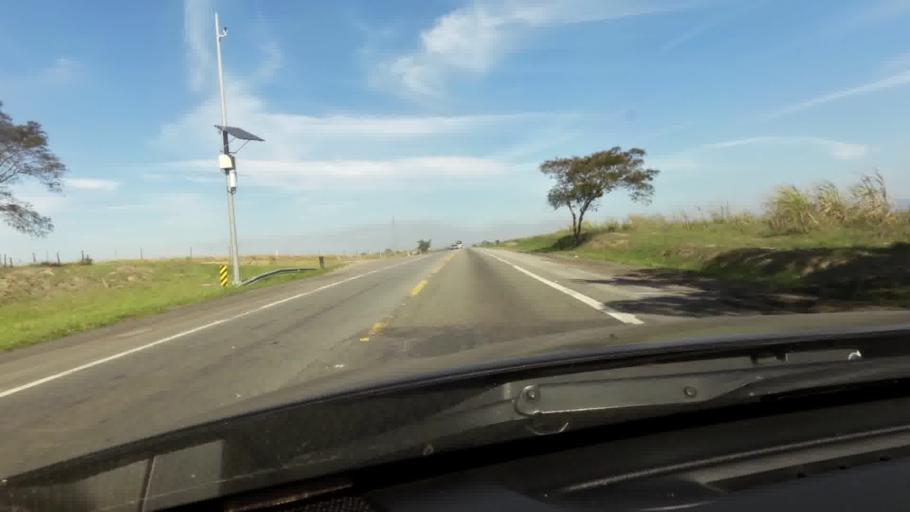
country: BR
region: Rio de Janeiro
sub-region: Campos Dos Goytacazes
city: Campos
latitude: -21.5263
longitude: -41.3373
